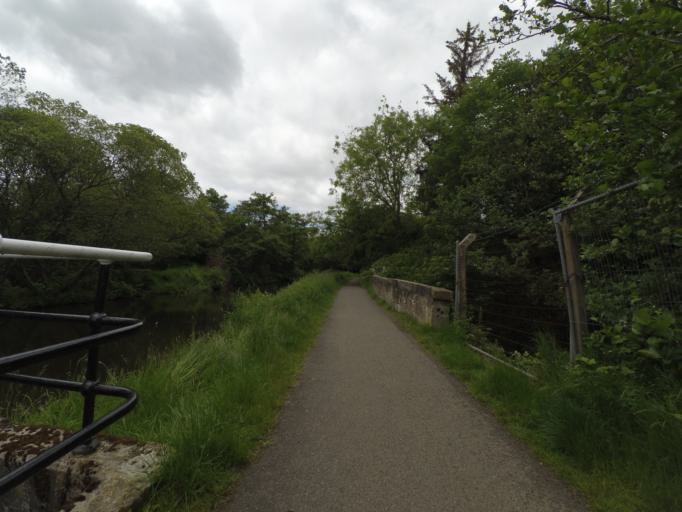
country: GB
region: Scotland
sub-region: Falkirk
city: Polmont
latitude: 55.9831
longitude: -3.7167
